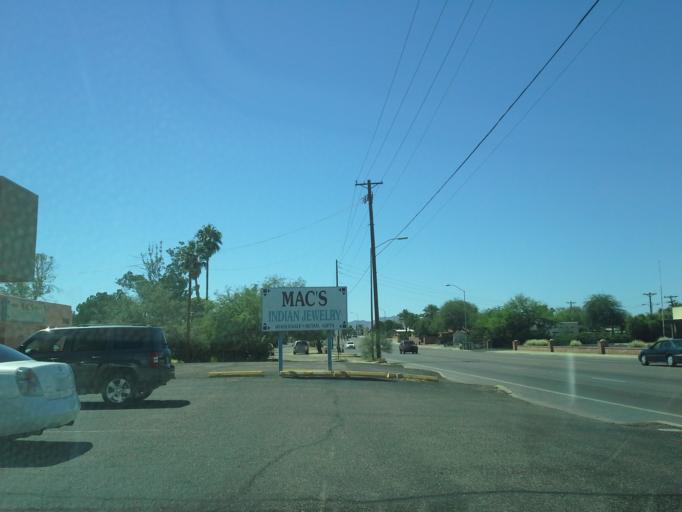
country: US
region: Arizona
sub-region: Pima County
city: Tucson
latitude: 32.2502
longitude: -110.9363
